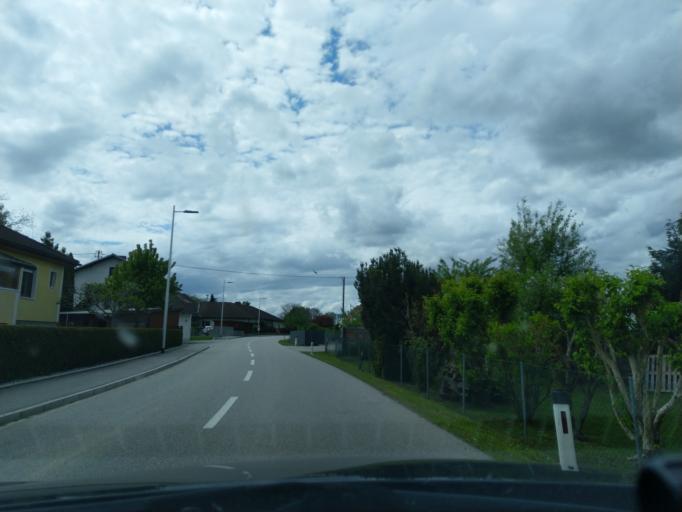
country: AT
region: Upper Austria
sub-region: Politischer Bezirk Scharding
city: Sankt Marienkirchen bei Schaerding
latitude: 48.3428
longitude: 13.3957
